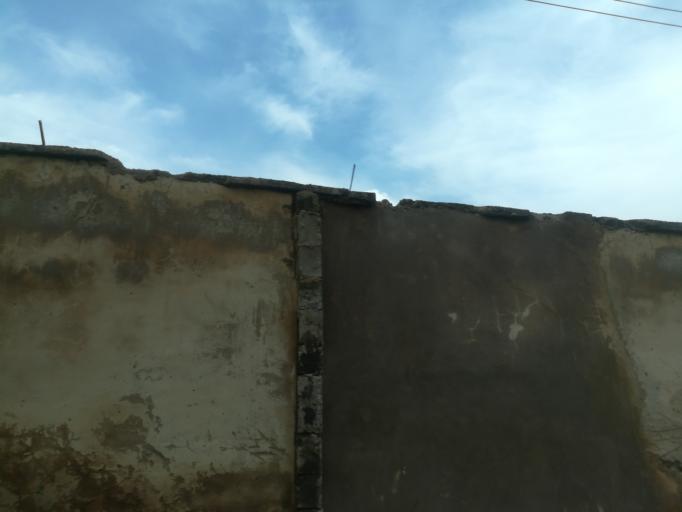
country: NG
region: Oyo
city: Ibadan
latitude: 7.4160
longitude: 3.9019
